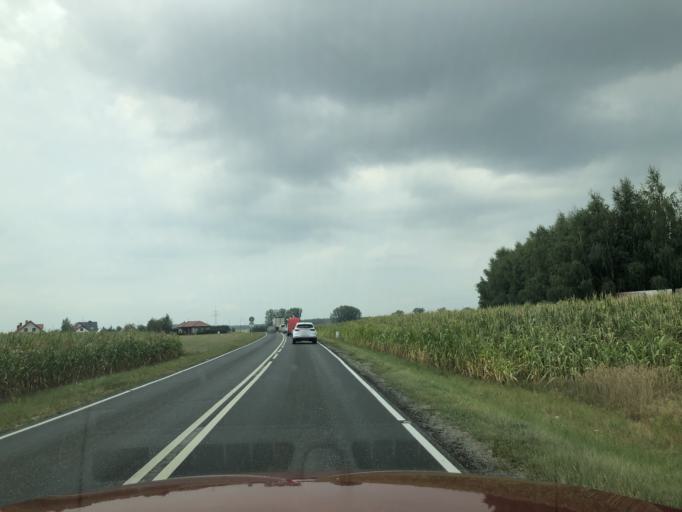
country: PL
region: Greater Poland Voivodeship
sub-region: Powiat leszczynski
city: Swieciechowa
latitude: 51.8614
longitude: 16.5035
